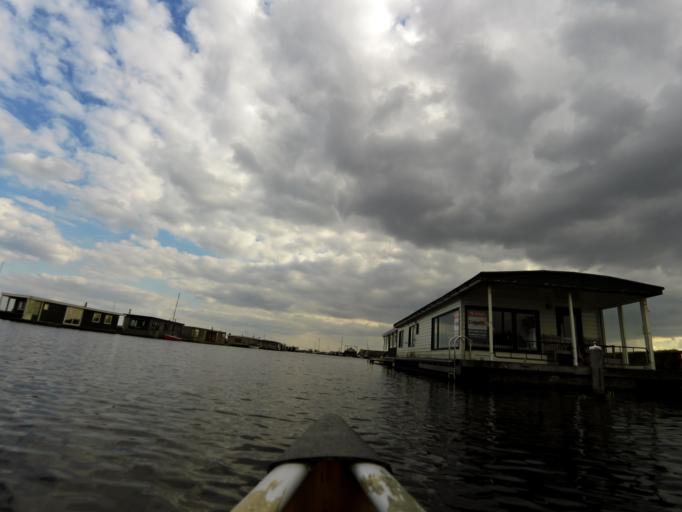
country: NL
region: South Holland
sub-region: Gemeente Teylingen
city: Sassenheim
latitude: 52.1941
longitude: 4.5361
